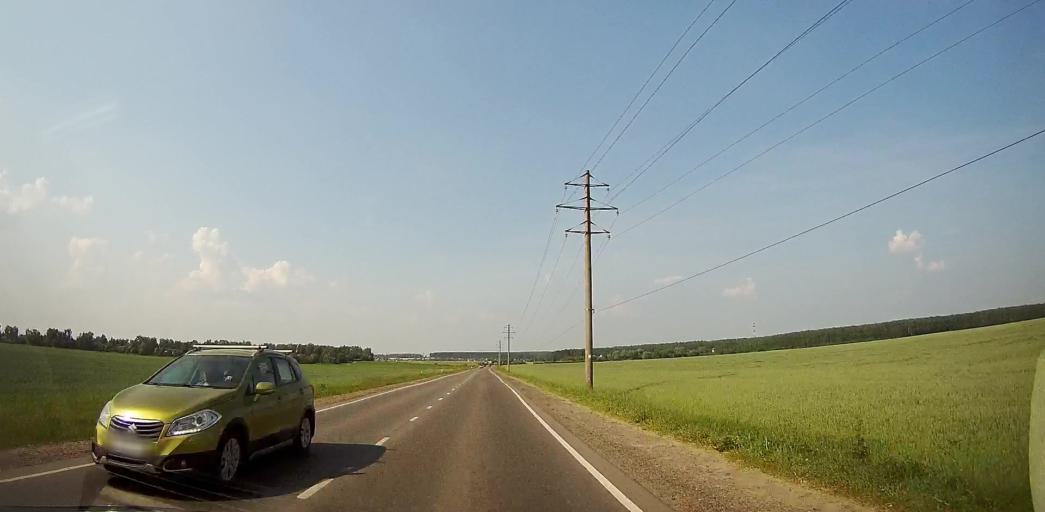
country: RU
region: Moskovskaya
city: Barybino
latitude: 55.2563
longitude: 37.9188
